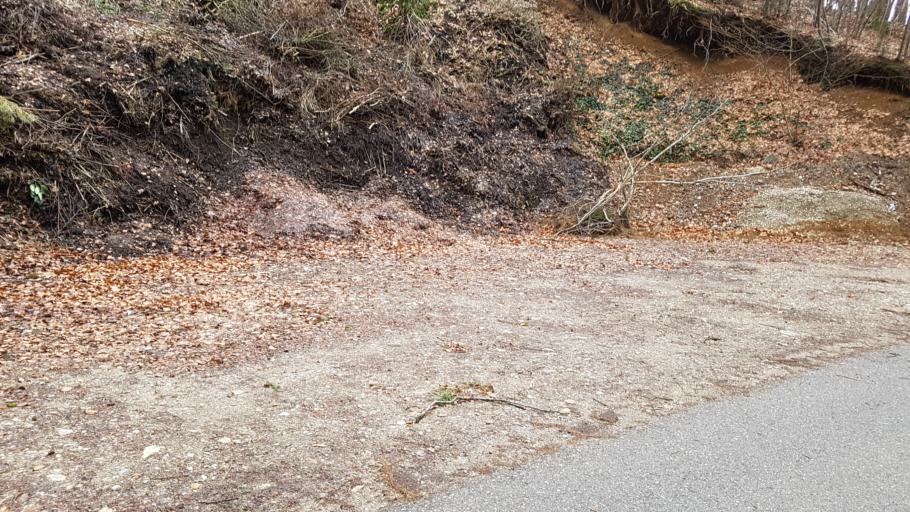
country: AT
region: Salzburg
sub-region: Politischer Bezirk Salzburg-Umgebung
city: Henndorf am Wallersee
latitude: 47.8987
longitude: 13.1688
